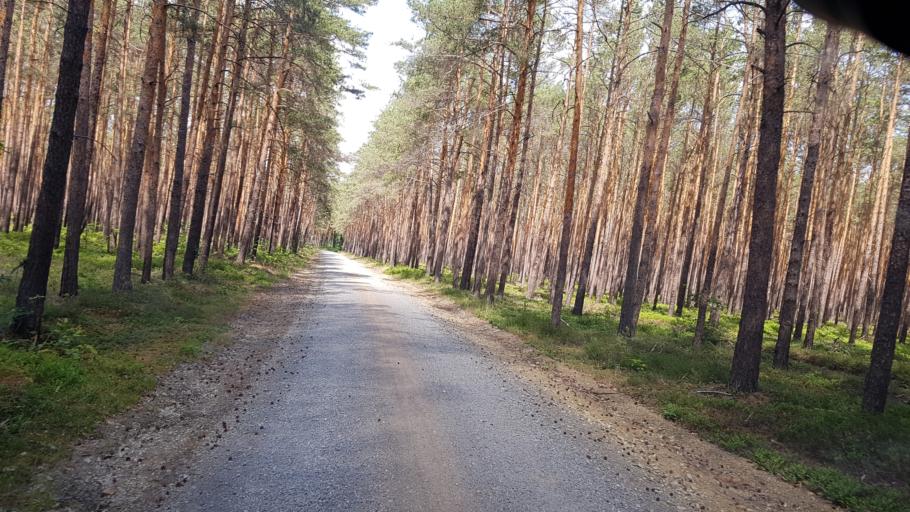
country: DE
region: Brandenburg
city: Ruckersdorf
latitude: 51.5801
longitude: 13.6073
